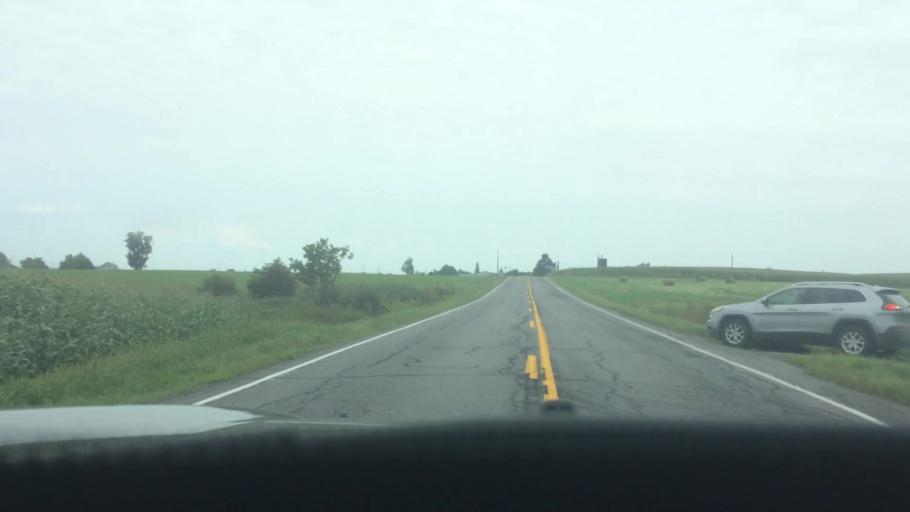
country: US
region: New York
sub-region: St. Lawrence County
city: Hannawa Falls
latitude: 44.6844
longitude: -74.7139
